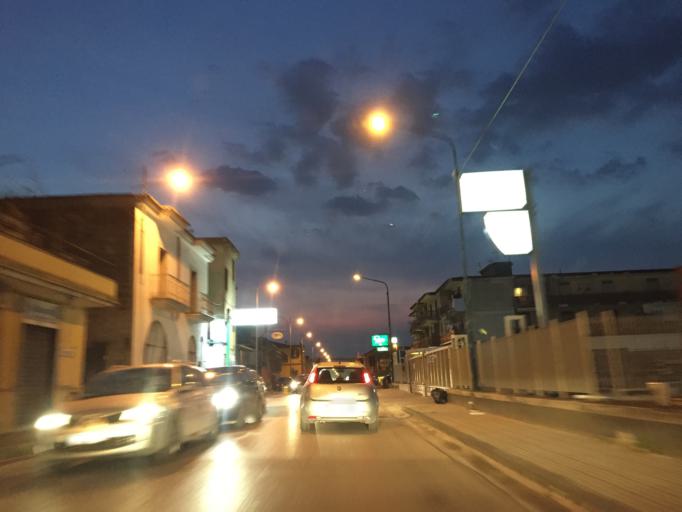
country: IT
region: Campania
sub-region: Provincia di Salerno
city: Sant'Egidio del Monte Albino
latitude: 40.7478
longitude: 14.5981
